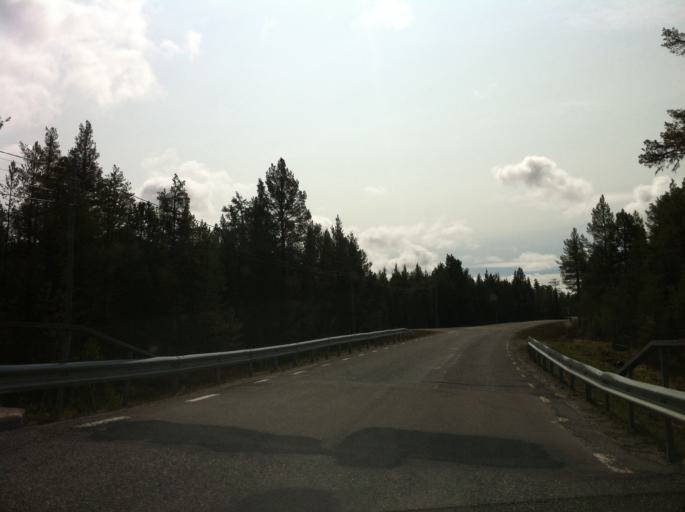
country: NO
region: Hedmark
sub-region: Engerdal
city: Engerdal
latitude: 62.4382
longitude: 12.6795
